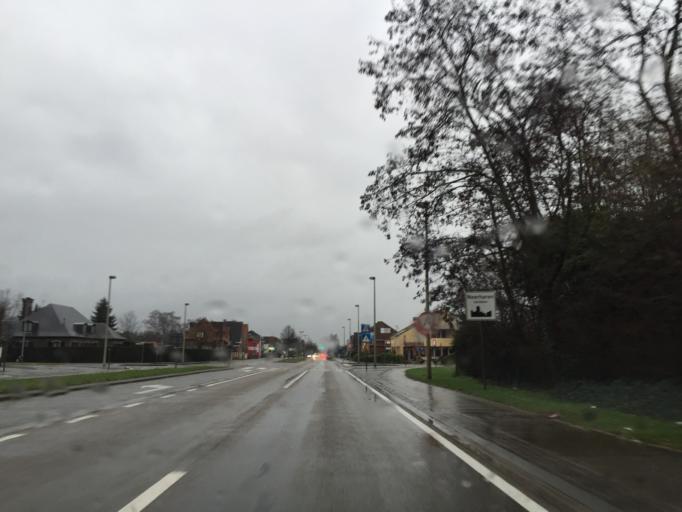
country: BE
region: Flanders
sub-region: Provincie Limburg
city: Lanaken
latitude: 50.9051
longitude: 5.6794
